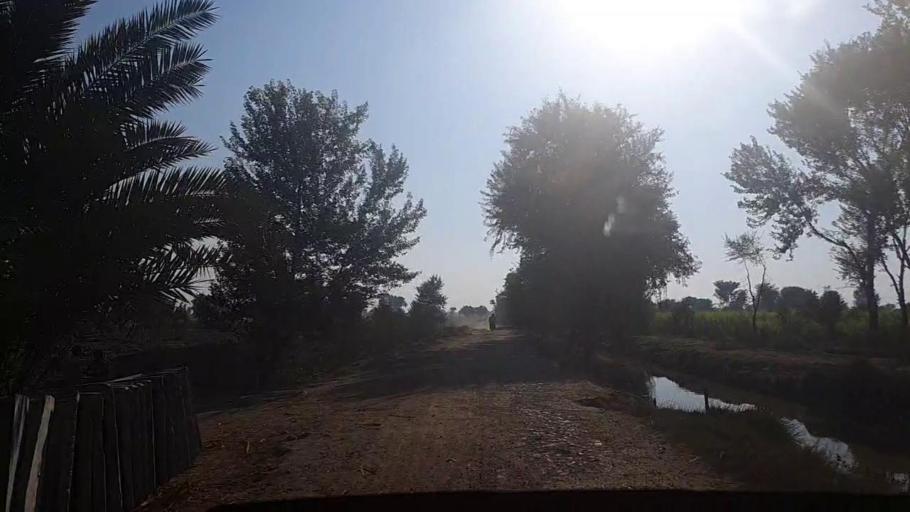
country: PK
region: Sindh
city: Gambat
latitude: 27.3742
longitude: 68.4657
